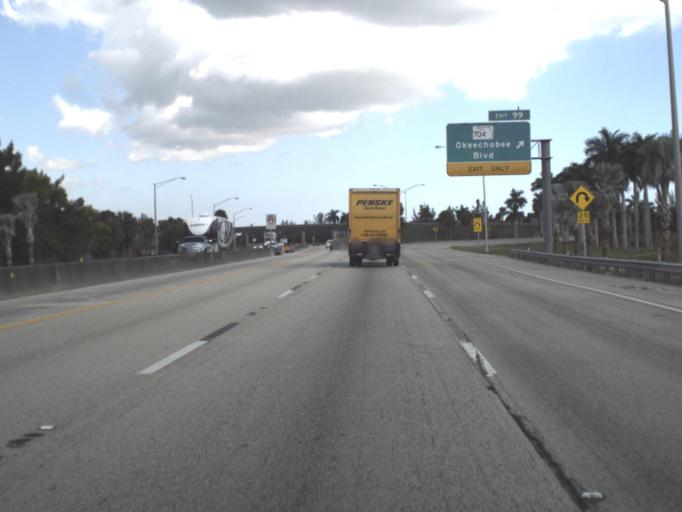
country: US
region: Florida
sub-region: Palm Beach County
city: Plantation Mobile Home Park
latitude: 26.7086
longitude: -80.1403
